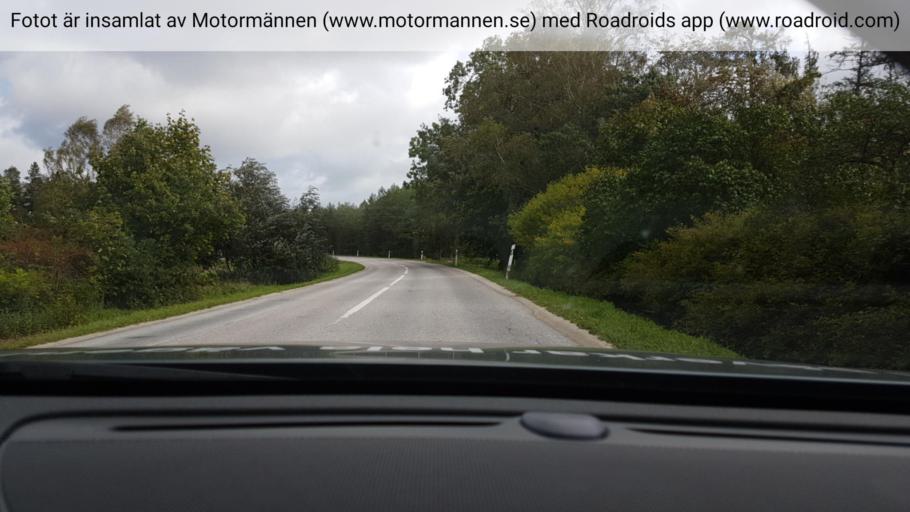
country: SE
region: Gotland
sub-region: Gotland
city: Visby
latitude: 57.6827
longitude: 18.4968
